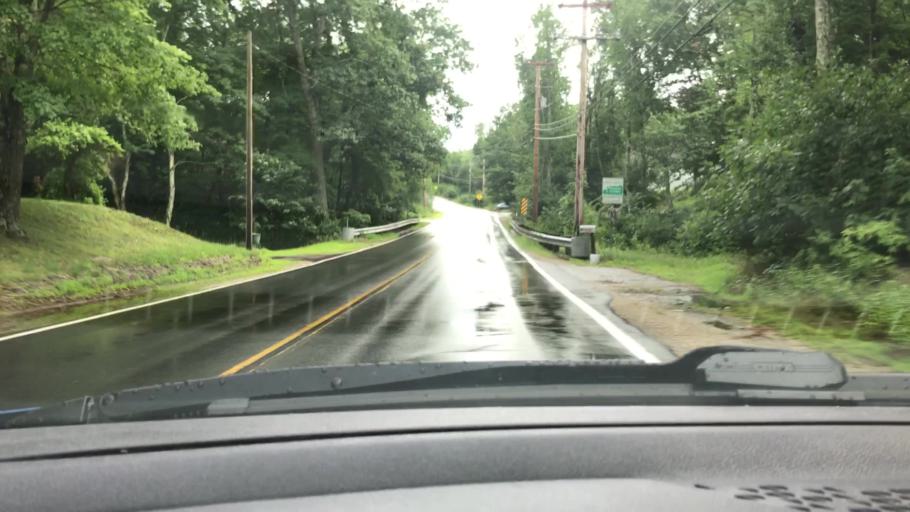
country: US
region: New Hampshire
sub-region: Merrimack County
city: Epsom
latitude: 43.2205
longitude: -71.2915
